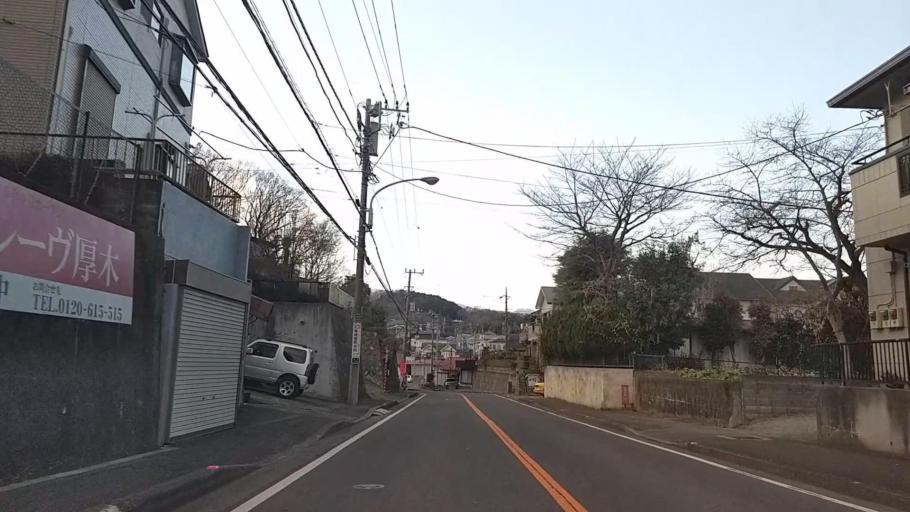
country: JP
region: Kanagawa
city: Atsugi
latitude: 35.4466
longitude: 139.3297
